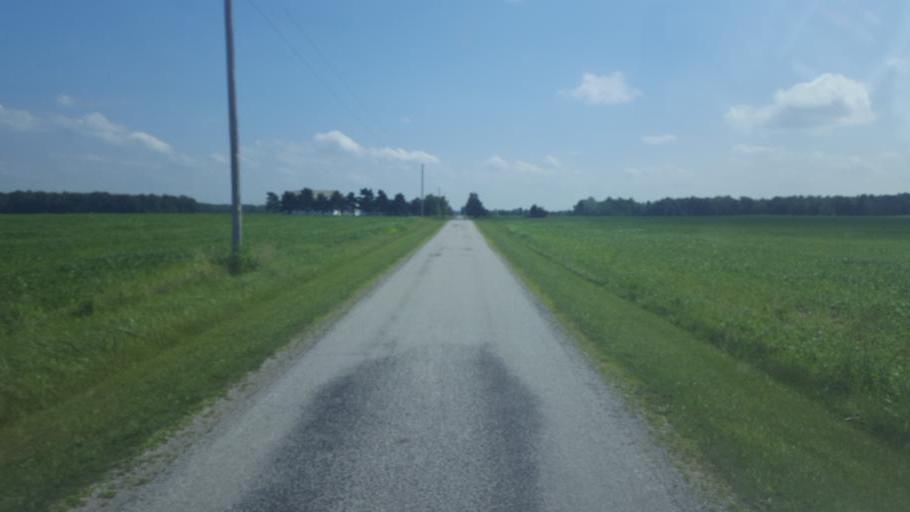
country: US
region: Ohio
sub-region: Huron County
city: Willard
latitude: 41.1088
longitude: -82.8165
